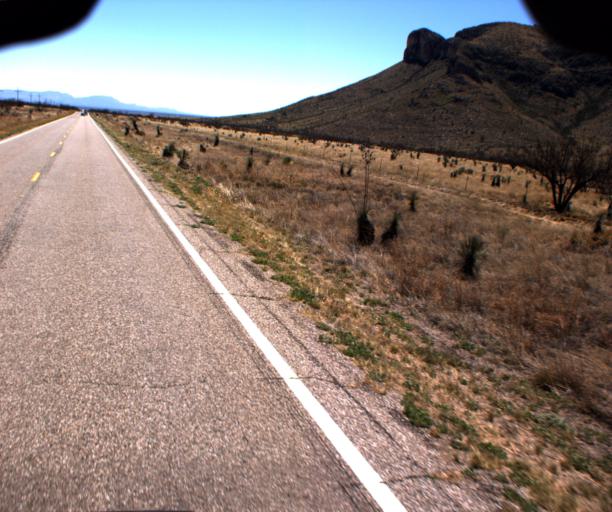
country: US
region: Arizona
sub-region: Cochise County
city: Huachuca City
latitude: 31.7044
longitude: -110.4370
